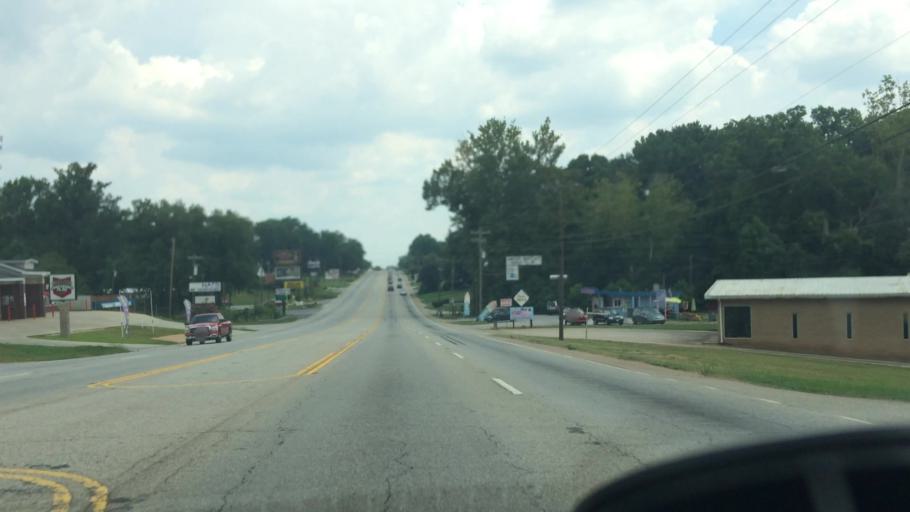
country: US
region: South Carolina
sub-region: Greenville County
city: Sans Souci
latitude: 34.9021
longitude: -82.4171
